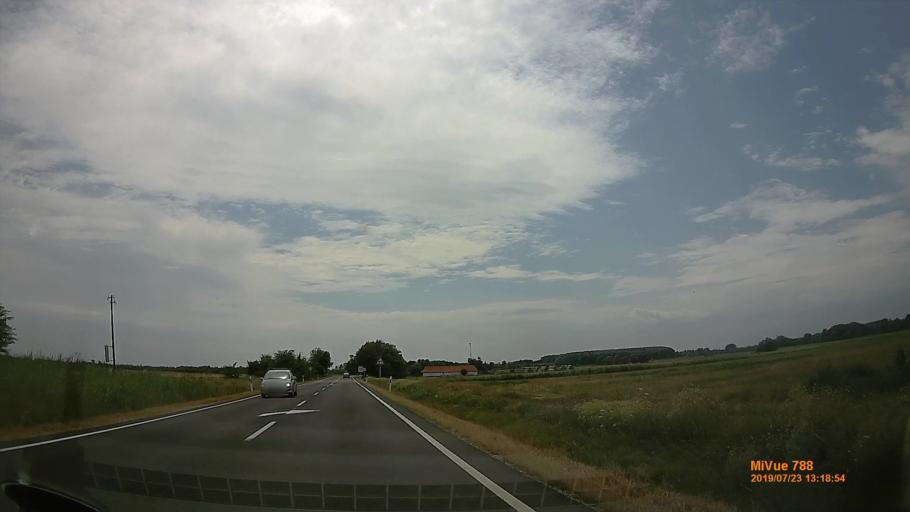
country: HU
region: Hajdu-Bihar
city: Polgar
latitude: 47.8794
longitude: 21.1457
